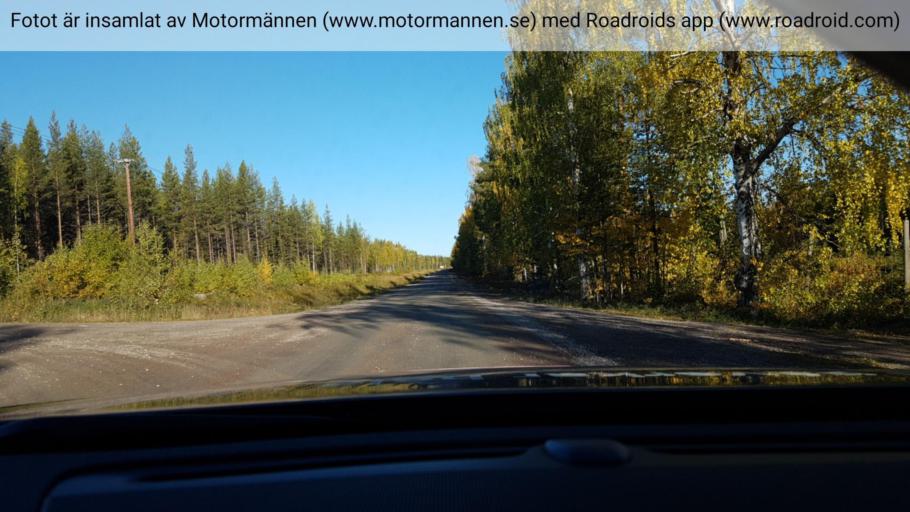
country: SE
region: Norrbotten
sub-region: Bodens Kommun
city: Boden
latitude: 66.1372
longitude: 21.2921
